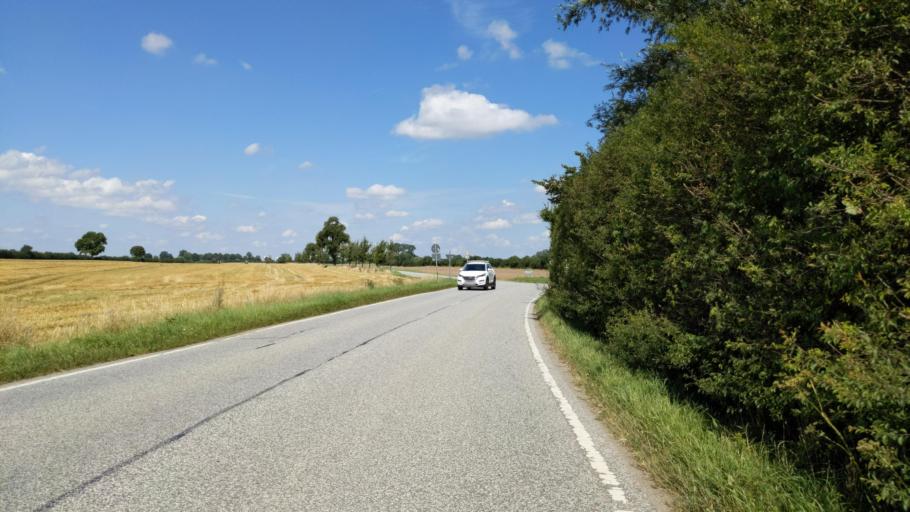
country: DE
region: Schleswig-Holstein
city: Krummesse
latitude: 53.8169
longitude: 10.6733
